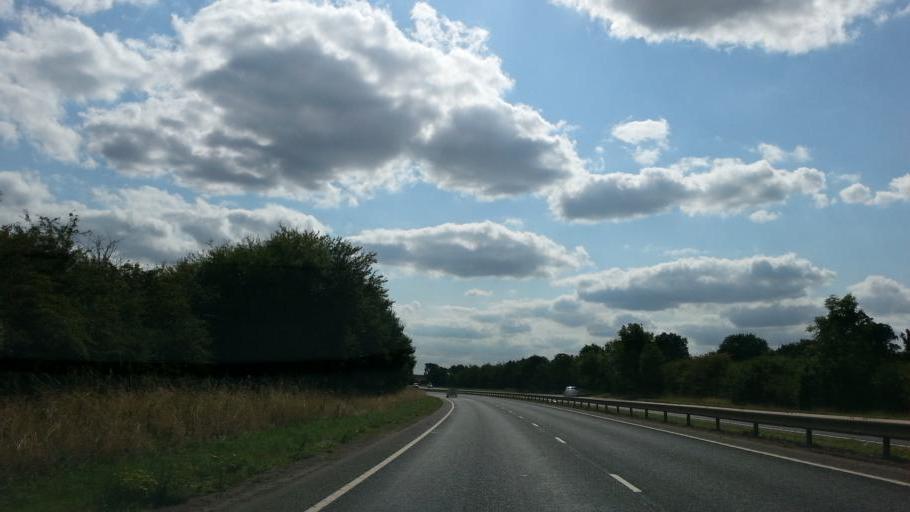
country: GB
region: England
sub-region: Leicestershire
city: Mountsorrel
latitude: 52.7050
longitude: -1.1257
